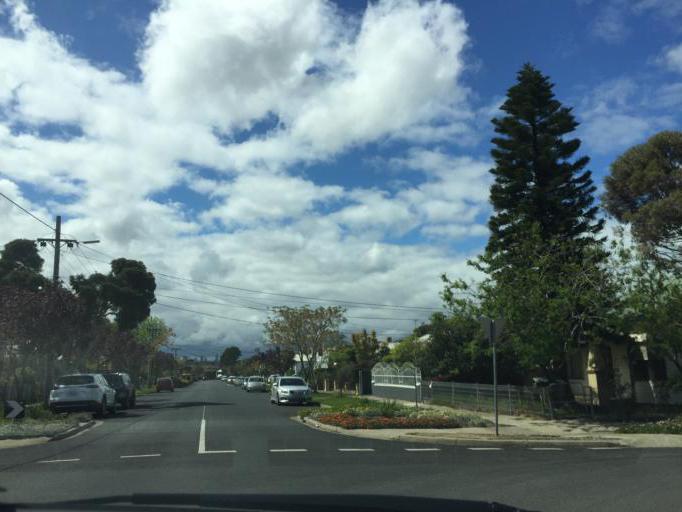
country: AU
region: Victoria
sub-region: Maribyrnong
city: West Footscray
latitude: -37.7990
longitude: 144.8747
